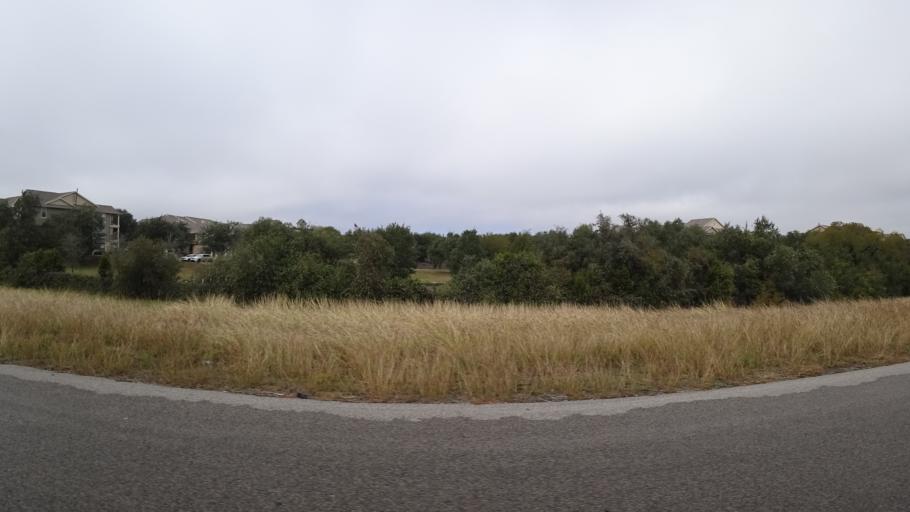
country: US
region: Texas
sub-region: Travis County
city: Shady Hollow
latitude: 30.2061
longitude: -97.8628
